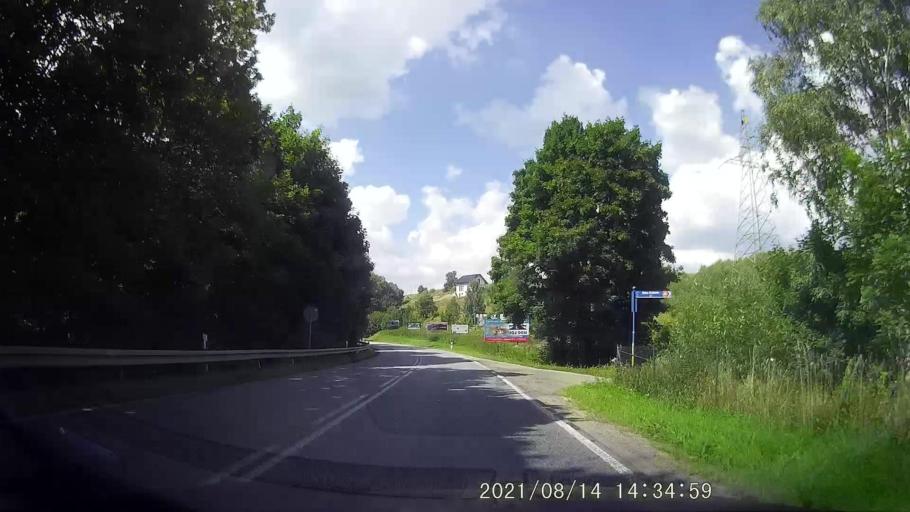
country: PL
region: Lower Silesian Voivodeship
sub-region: Powiat klodzki
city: Nowa Ruda
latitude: 50.5711
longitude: 16.5323
